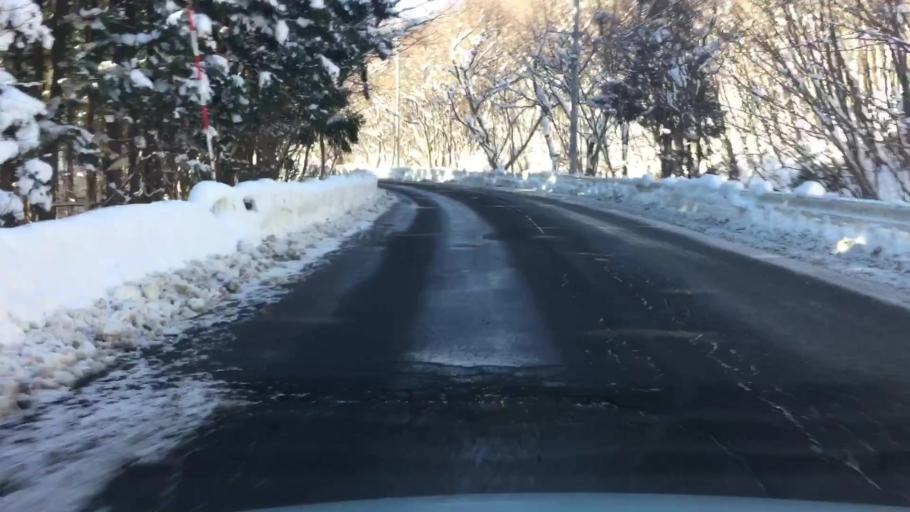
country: JP
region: Gunma
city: Numata
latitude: 36.7457
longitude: 138.9512
